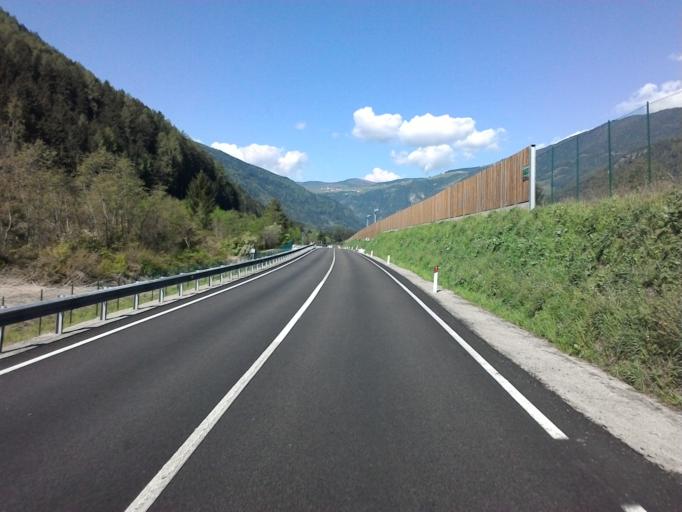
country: IT
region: Trentino-Alto Adige
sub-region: Bolzano
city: Terento
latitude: 46.8101
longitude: 11.7566
